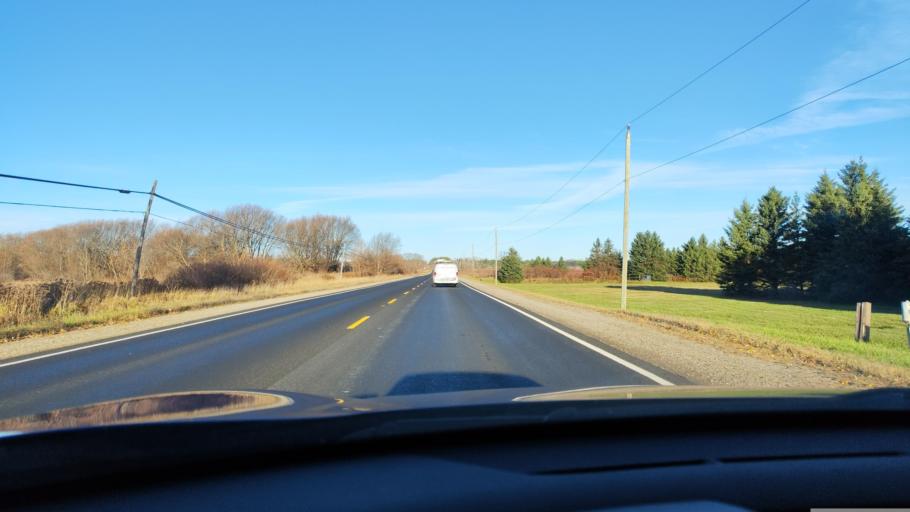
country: CA
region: Ontario
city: Angus
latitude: 44.3332
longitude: -79.9237
